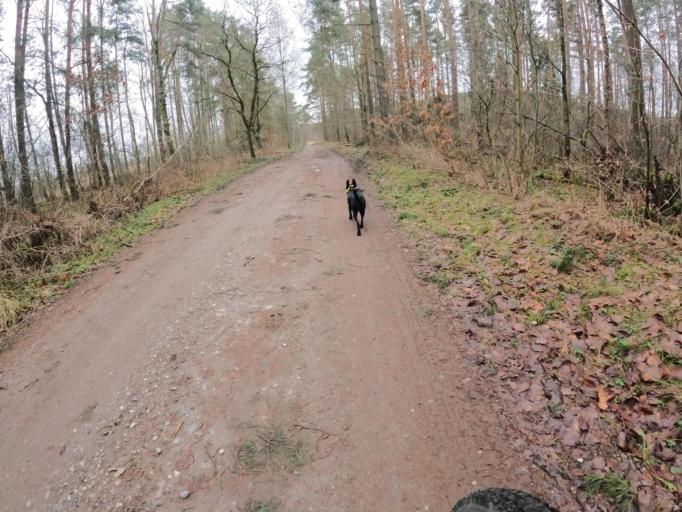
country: PL
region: West Pomeranian Voivodeship
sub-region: Powiat slawienski
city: Slawno
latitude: 54.2500
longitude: 16.6421
